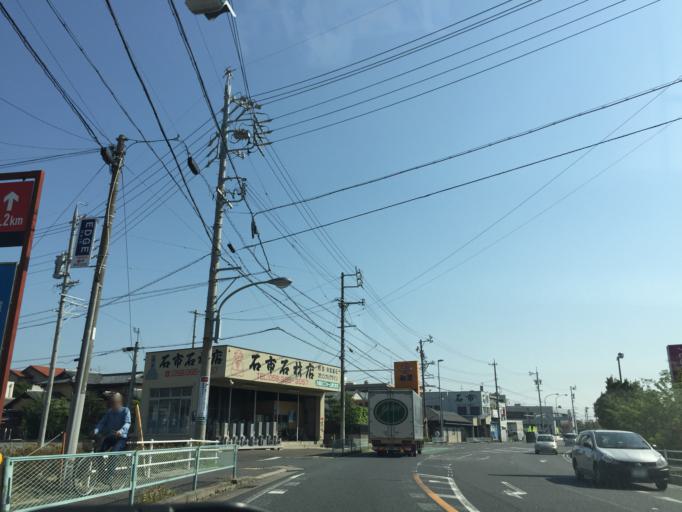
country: JP
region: Mie
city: Yokkaichi
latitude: 35.0079
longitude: 136.6543
